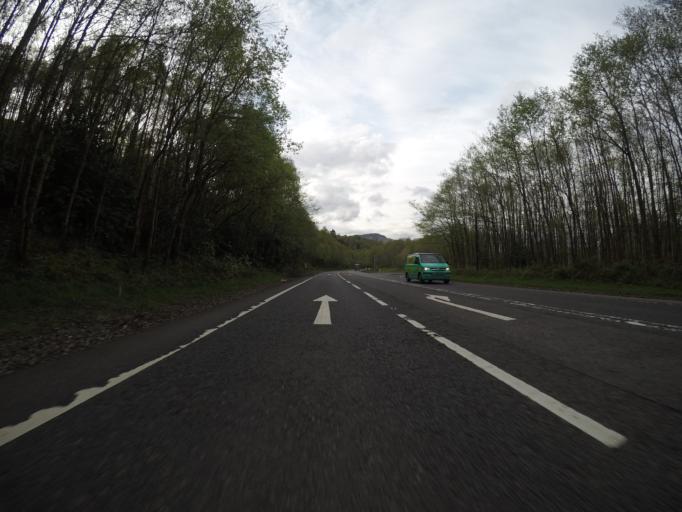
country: GB
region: Scotland
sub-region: Argyll and Bute
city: Garelochhead
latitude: 56.1853
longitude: -4.6961
